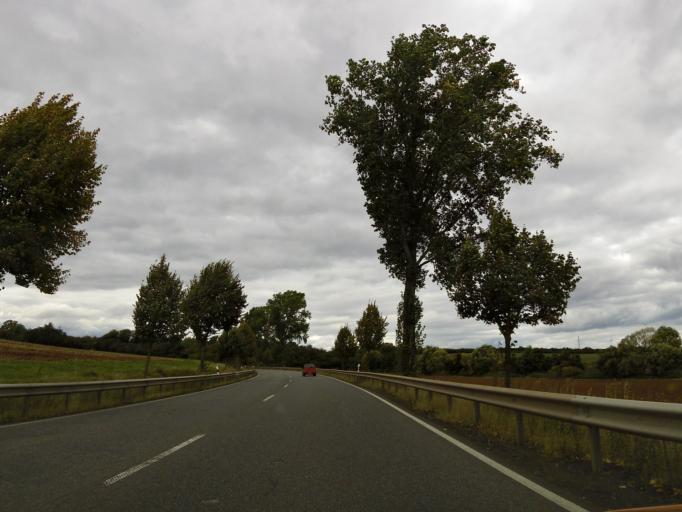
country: DE
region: Rheinland-Pfalz
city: Dreisen
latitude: 49.5993
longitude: 8.0231
